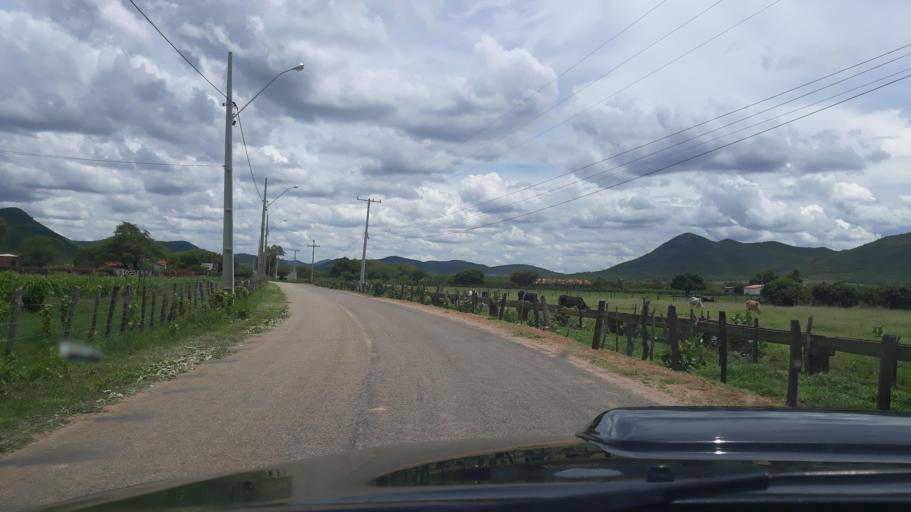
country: BR
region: Bahia
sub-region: Guanambi
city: Guanambi
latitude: -14.2930
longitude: -42.6971
